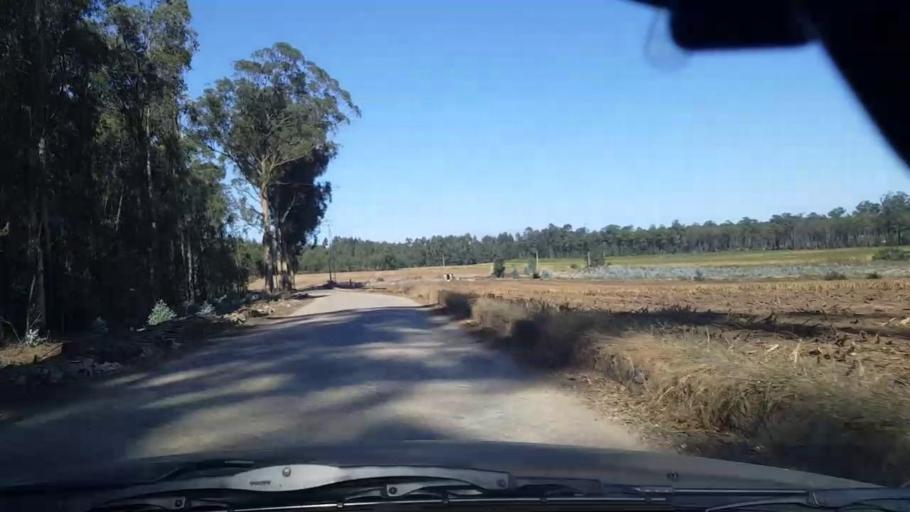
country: PT
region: Braga
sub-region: Vila Nova de Famalicao
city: Ribeirao
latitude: 41.3857
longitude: -8.6365
